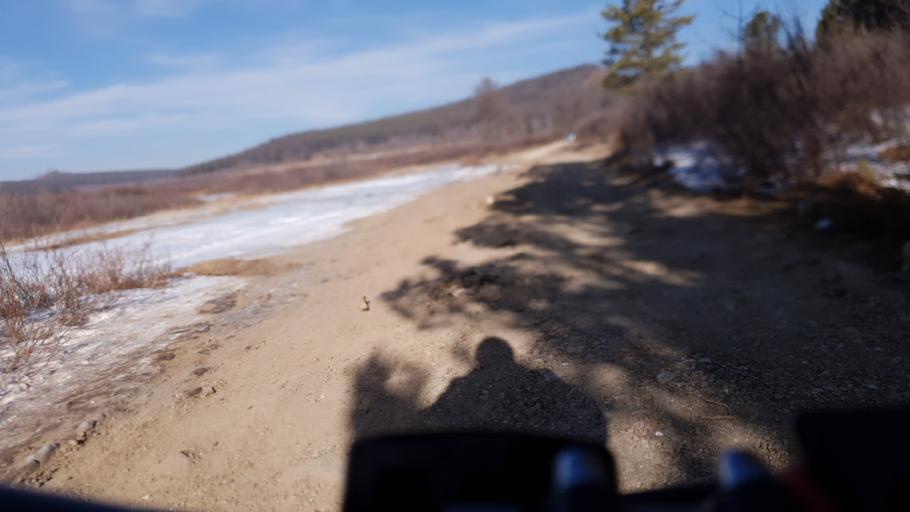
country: MN
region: Ulaanbaatar
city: Ulaanbaatar
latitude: 48.1598
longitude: 106.8826
